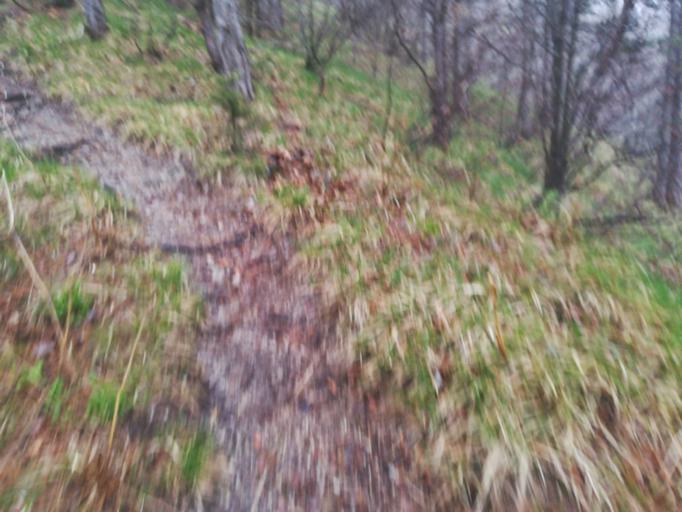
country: HR
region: Varazdinska
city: Ivanec
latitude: 46.1902
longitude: 16.1391
